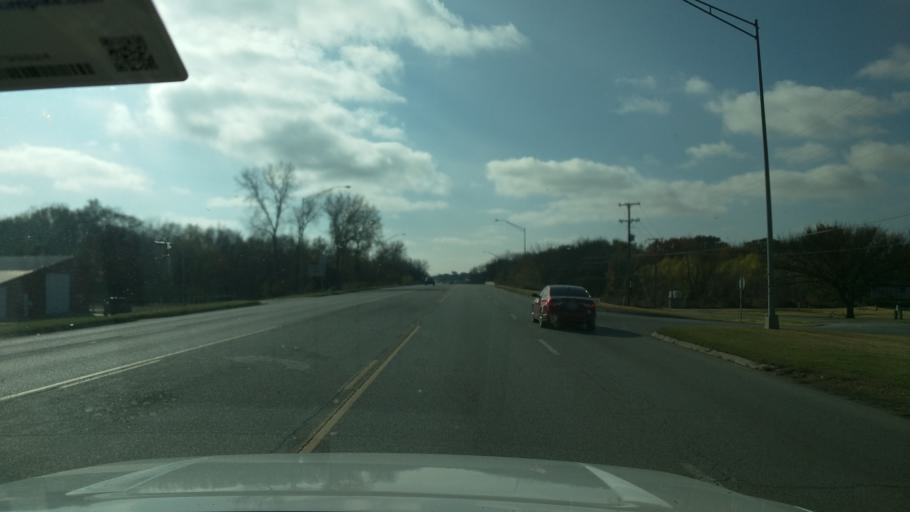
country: US
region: Oklahoma
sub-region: Washington County
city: Dewey
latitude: 36.7845
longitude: -95.9352
